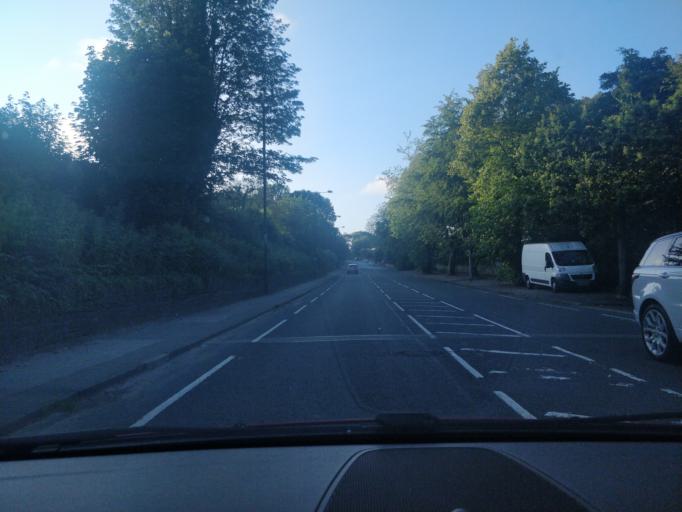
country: GB
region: England
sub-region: Lancashire
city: Appley Bridge
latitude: 53.5435
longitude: -2.7240
